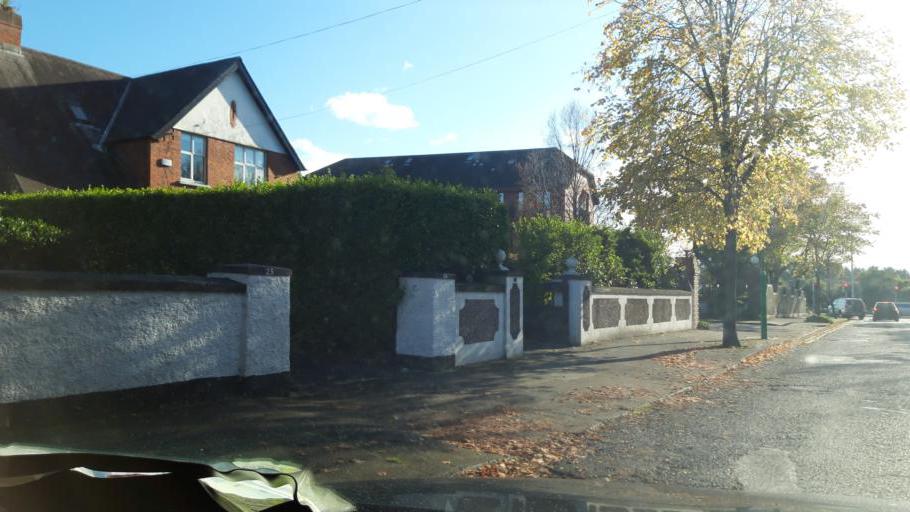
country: IE
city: Donnycarney
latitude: 53.3611
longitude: -6.2092
